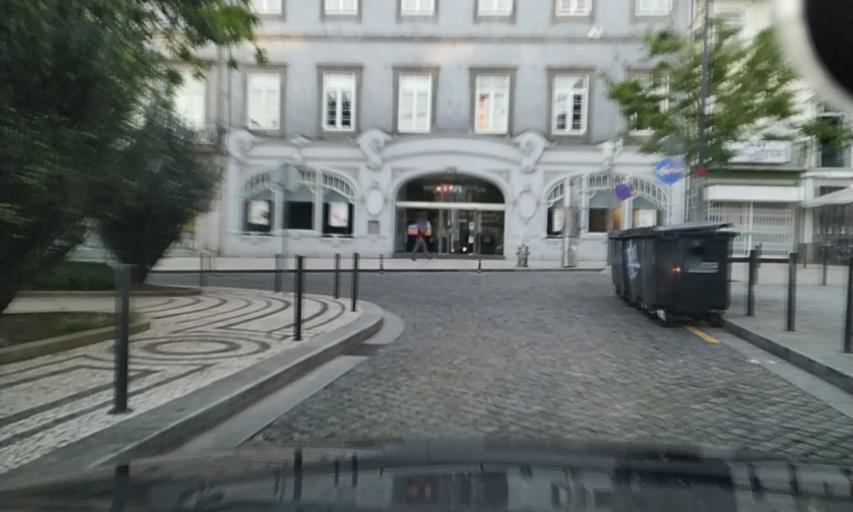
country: PT
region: Porto
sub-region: Porto
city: Porto
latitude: 41.1488
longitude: -8.6160
